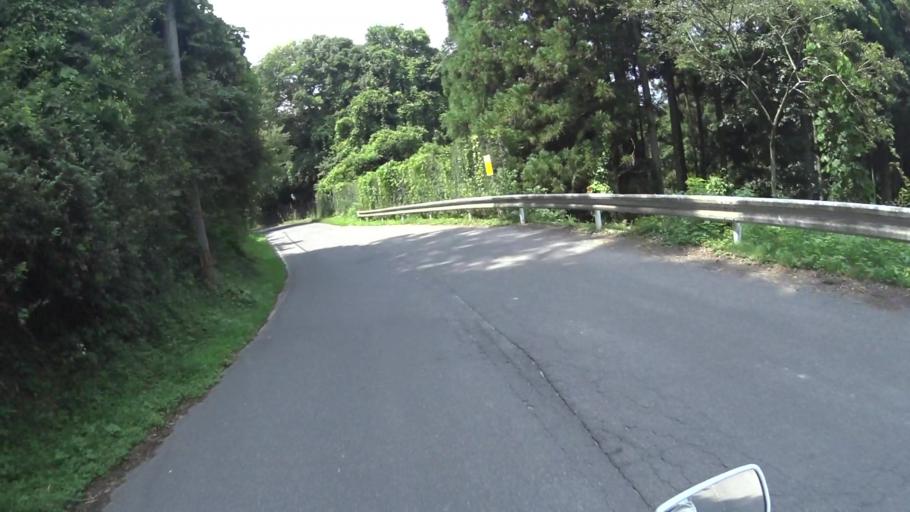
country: JP
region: Mie
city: Ueno-ebisumachi
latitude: 34.8158
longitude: 136.1223
